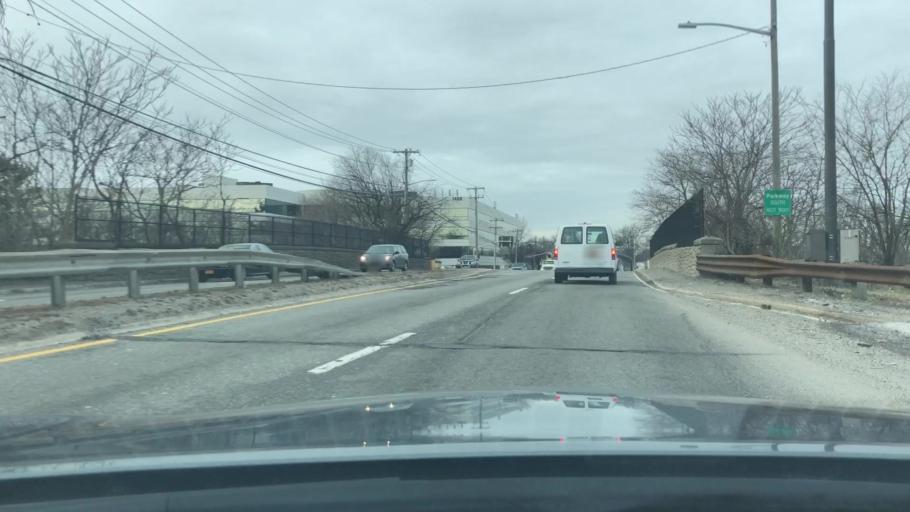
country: US
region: New York
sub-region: Nassau County
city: Salisbury
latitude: 40.7567
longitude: -73.5499
